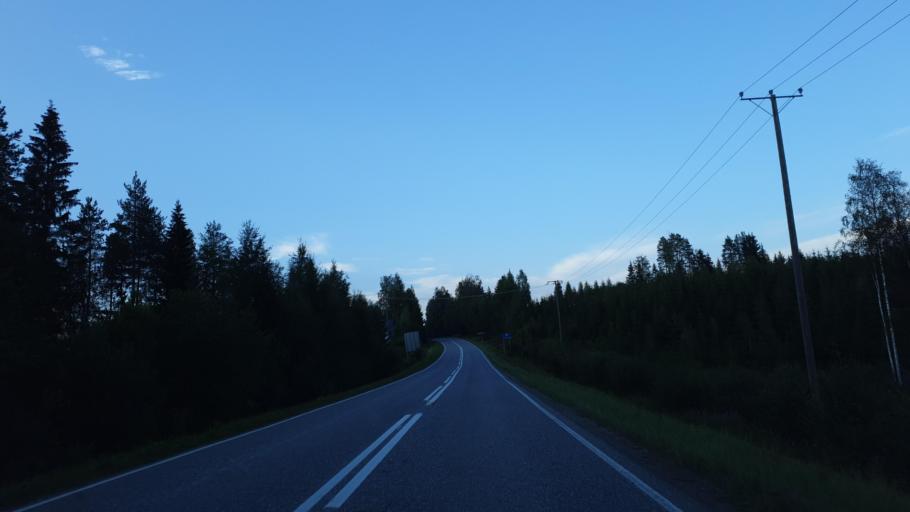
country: FI
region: Northern Savo
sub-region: Koillis-Savo
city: Kaavi
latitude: 62.9685
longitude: 28.7674
